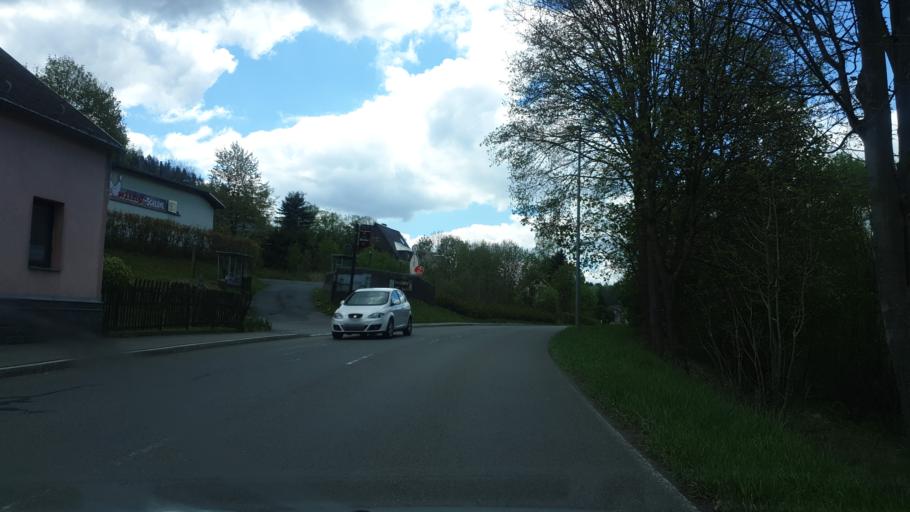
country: DE
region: Saxony
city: Klingenthal
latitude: 50.3749
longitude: 12.4755
